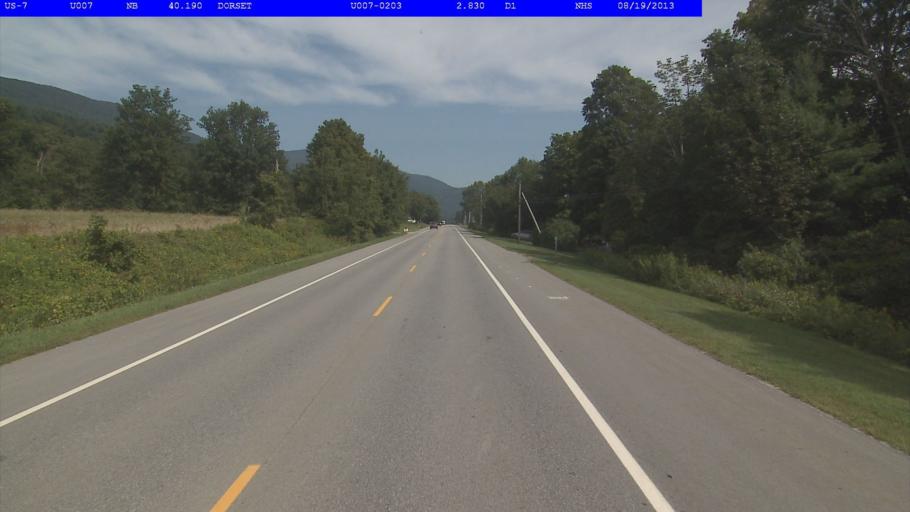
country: US
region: Vermont
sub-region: Bennington County
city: Manchester Center
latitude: 43.2498
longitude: -73.0079
